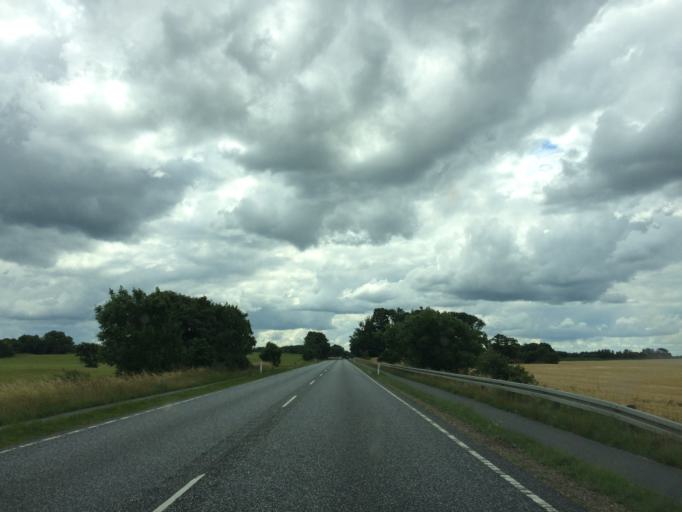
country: DK
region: Central Jutland
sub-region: Viborg Kommune
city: Viborg
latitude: 56.5237
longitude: 9.4583
